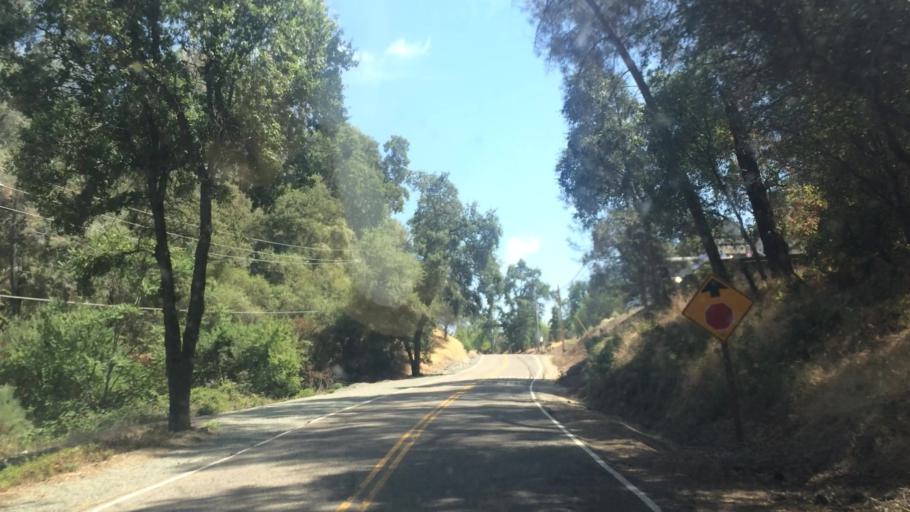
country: US
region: California
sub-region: Amador County
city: Sutter Creek
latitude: 38.3851
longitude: -120.8002
